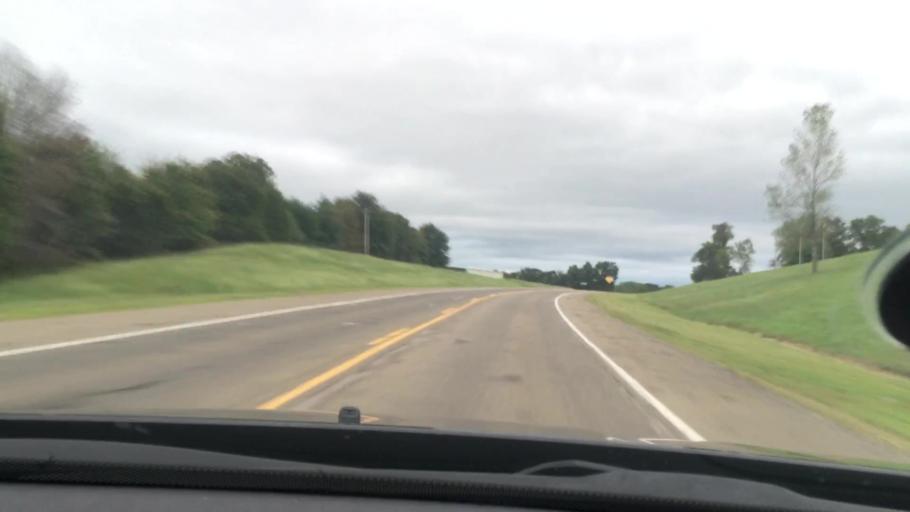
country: US
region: Oklahoma
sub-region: Sequoyah County
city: Vian
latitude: 35.5146
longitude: -94.9703
